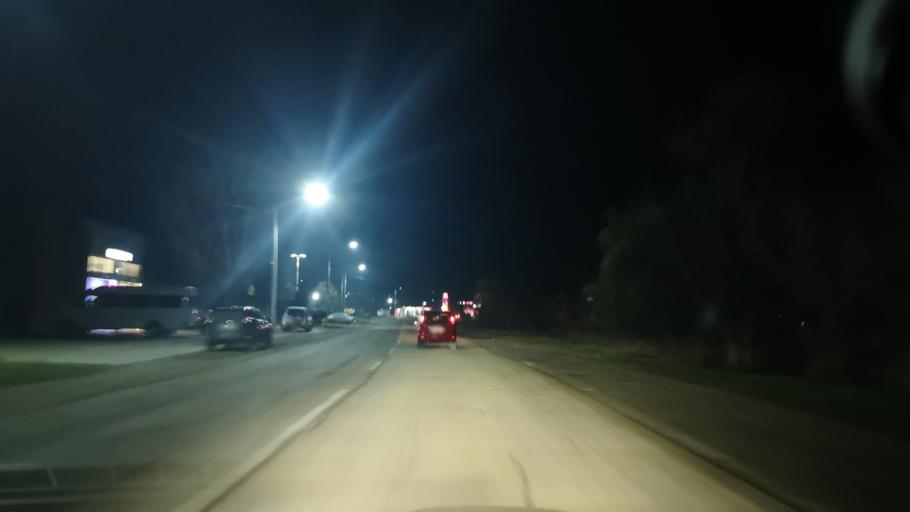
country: MD
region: Orhei
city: Orhei
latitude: 47.3720
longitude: 28.8164
